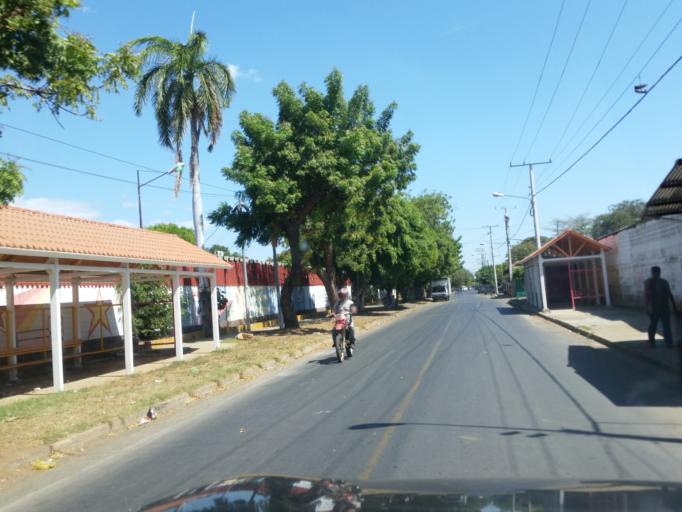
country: NI
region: Managua
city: Managua
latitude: 12.1598
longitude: -86.2891
